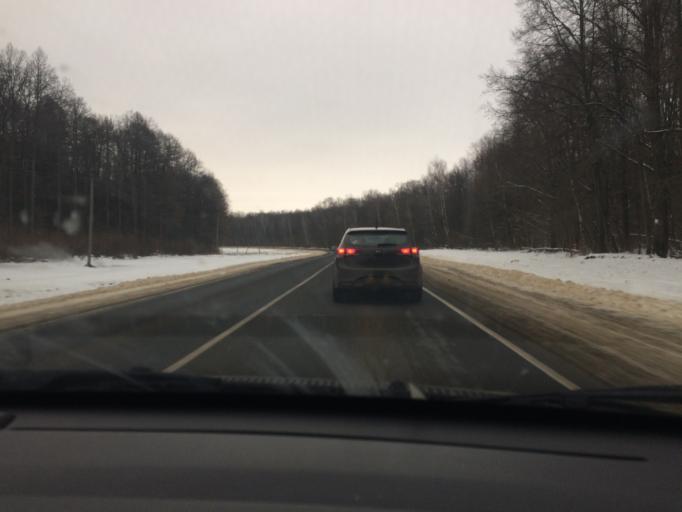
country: RU
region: Tula
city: Venev
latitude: 54.3354
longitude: 38.0973
